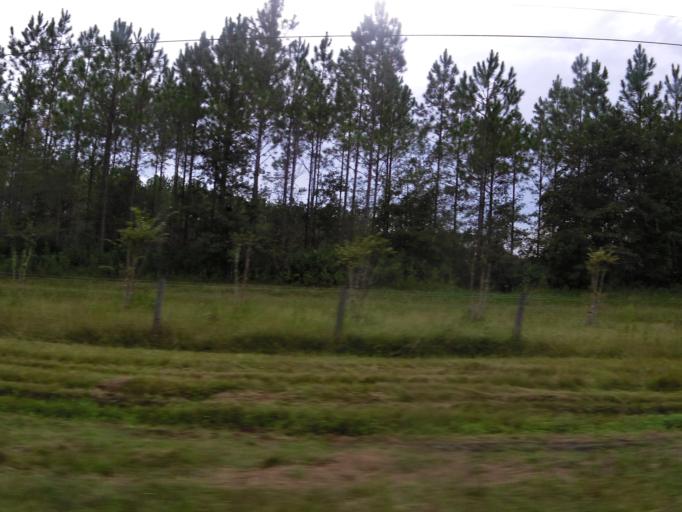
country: US
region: Florida
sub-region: Duval County
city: Baldwin
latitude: 30.3604
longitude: -81.9174
